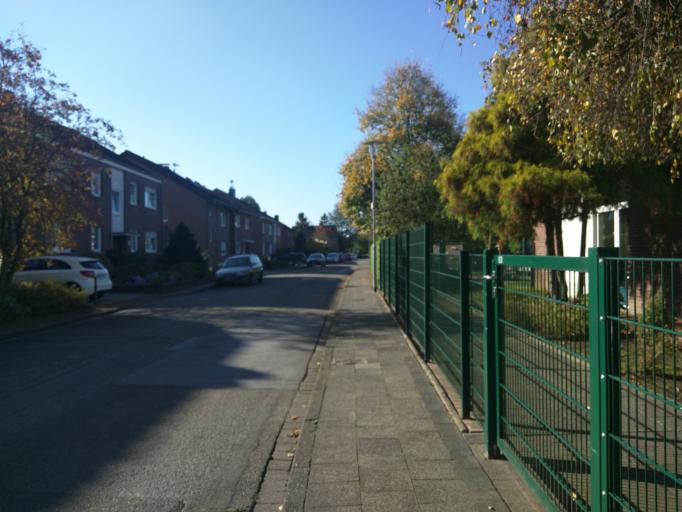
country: DE
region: North Rhine-Westphalia
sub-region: Regierungsbezirk Dusseldorf
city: Wachtendonk
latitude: 51.4538
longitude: 6.3729
